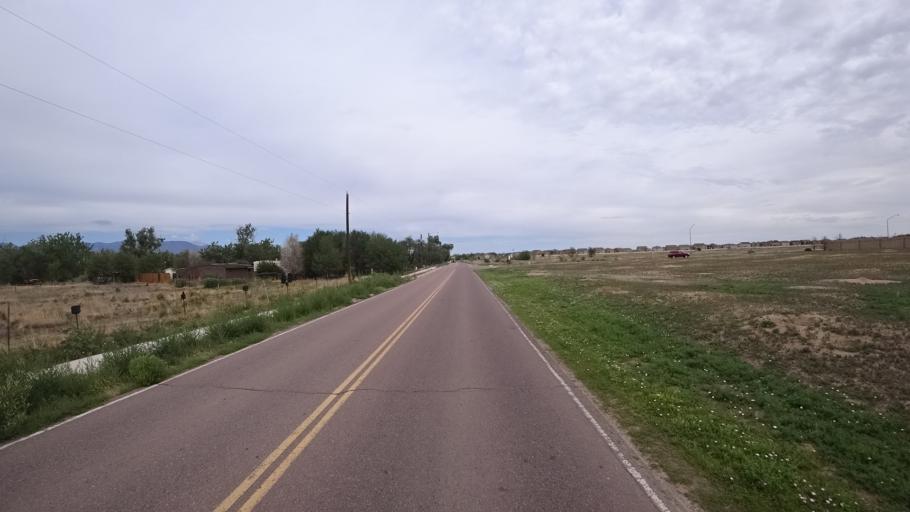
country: US
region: Colorado
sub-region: El Paso County
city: Fountain
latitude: 38.6670
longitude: -104.6936
